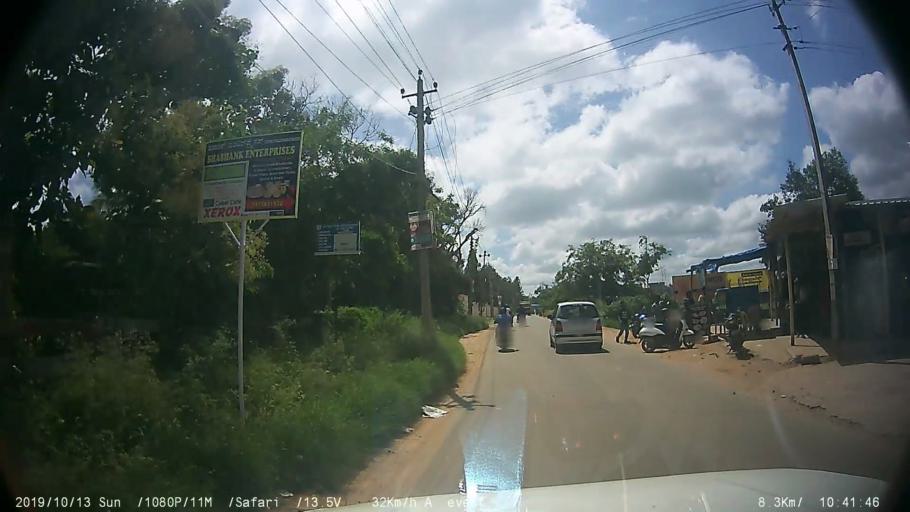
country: IN
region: Karnataka
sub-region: Bangalore Urban
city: Anekal
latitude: 12.8251
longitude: 77.6503
